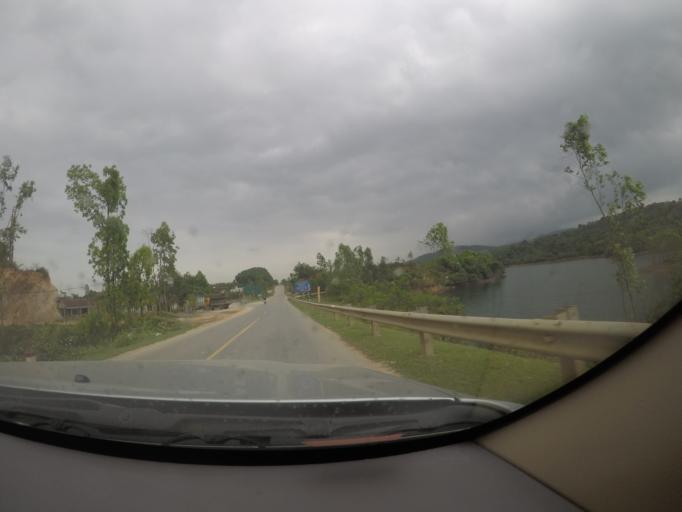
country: VN
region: Quang Binh
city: Ba Don
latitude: 17.6178
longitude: 106.3797
